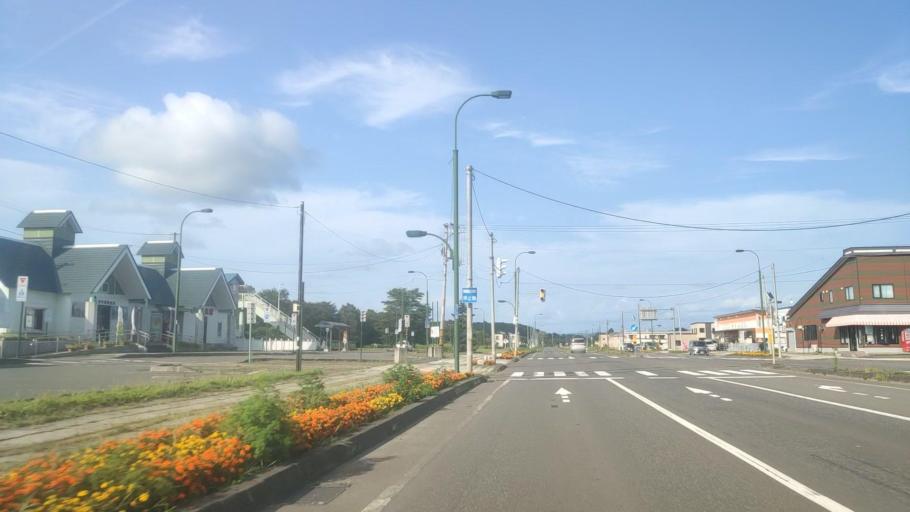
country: JP
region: Hokkaido
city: Chitose
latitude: 42.7649
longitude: 141.8143
